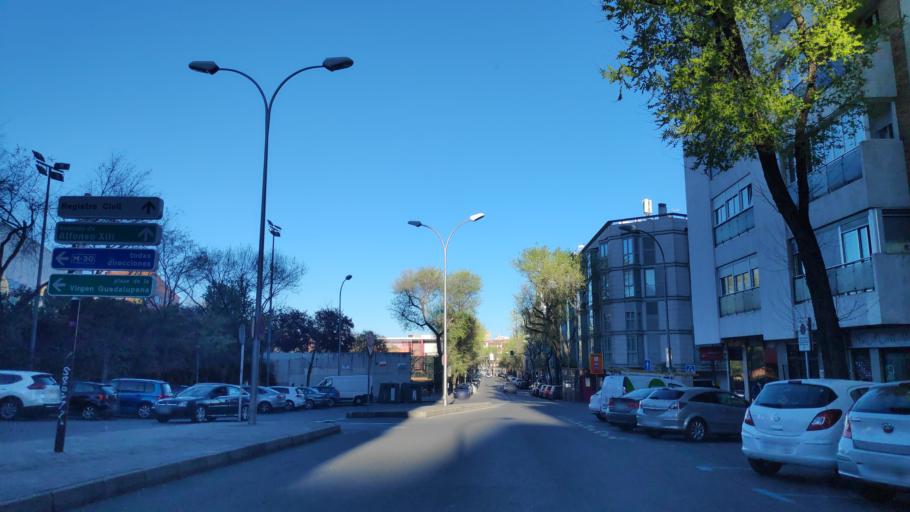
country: ES
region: Madrid
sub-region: Provincia de Madrid
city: Chamartin
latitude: 40.4487
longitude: -3.6737
